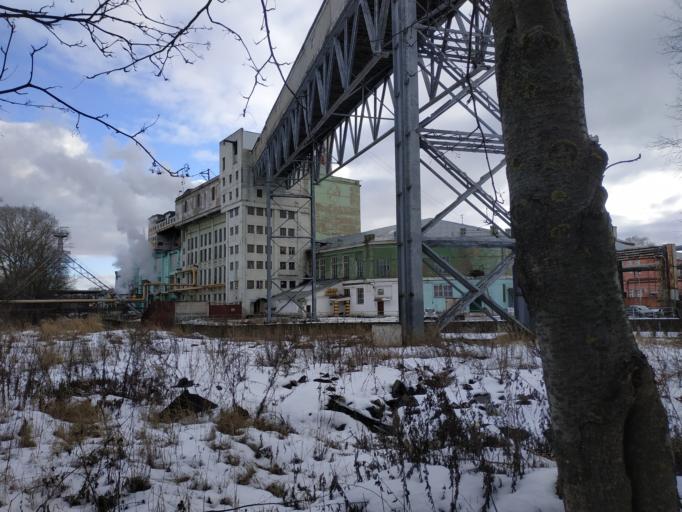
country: RU
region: Tverskaya
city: Tver
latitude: 56.8534
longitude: 35.8551
